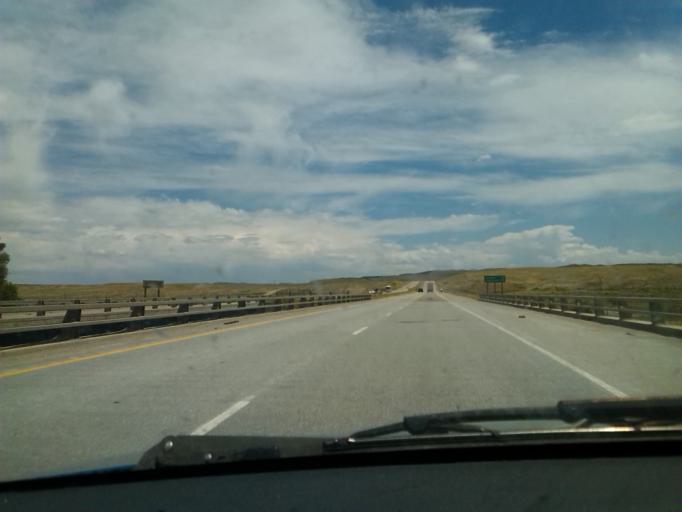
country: US
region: Wyoming
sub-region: Carbon County
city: Rawlins
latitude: 41.7510
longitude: -106.9490
